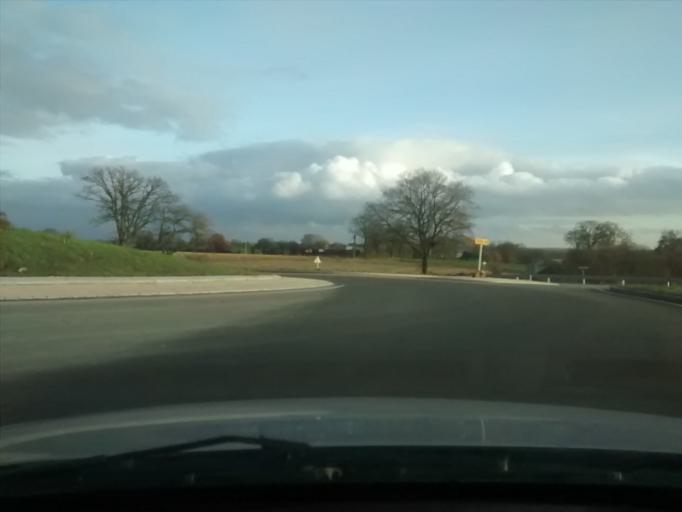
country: FR
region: Pays de la Loire
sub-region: Departement de la Mayenne
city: Loiron
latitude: 48.0715
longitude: -0.8943
